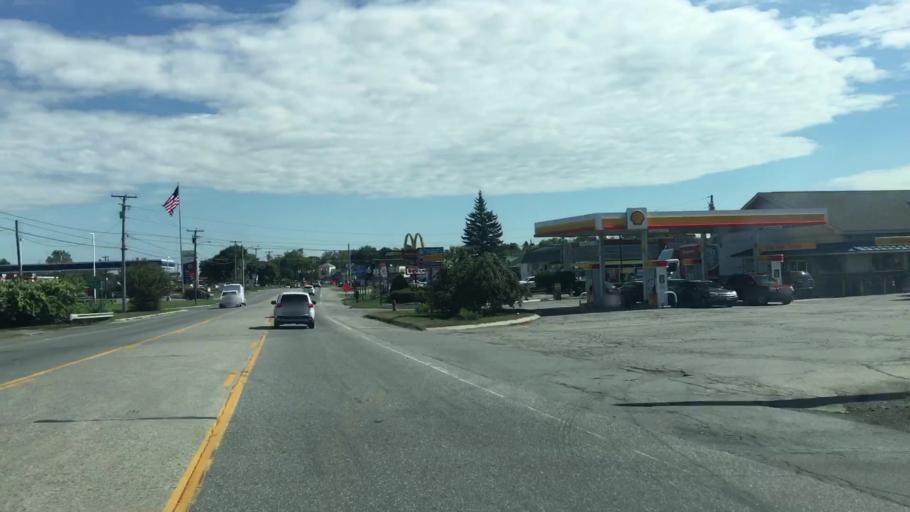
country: US
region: Maine
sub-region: Penobscot County
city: Newport
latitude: 44.8356
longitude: -69.2892
